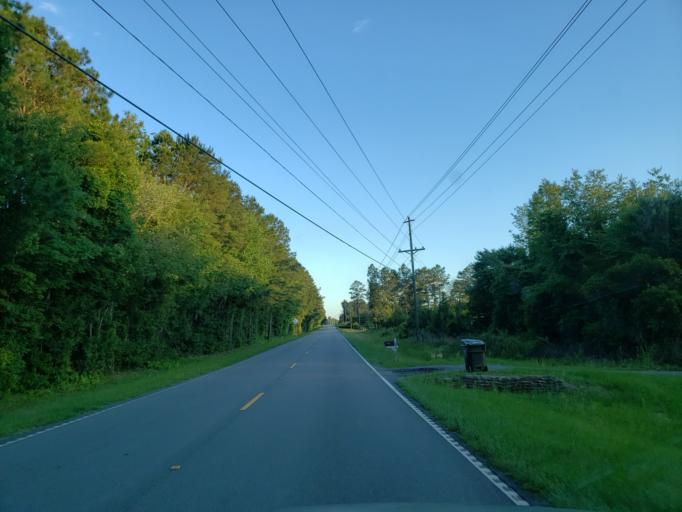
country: US
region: Georgia
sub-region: Lowndes County
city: Valdosta
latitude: 30.7100
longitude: -83.2421
